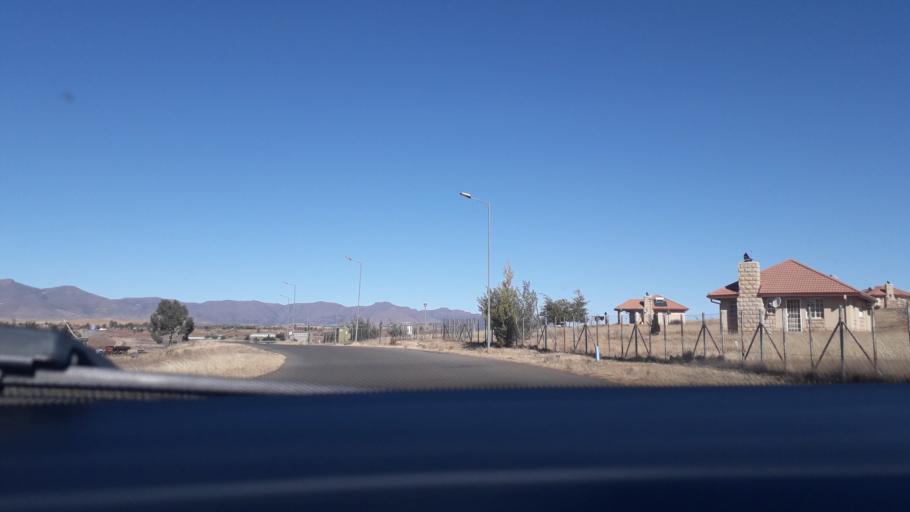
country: LS
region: Berea
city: Teyateyaneng
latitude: -29.3282
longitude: 27.7728
